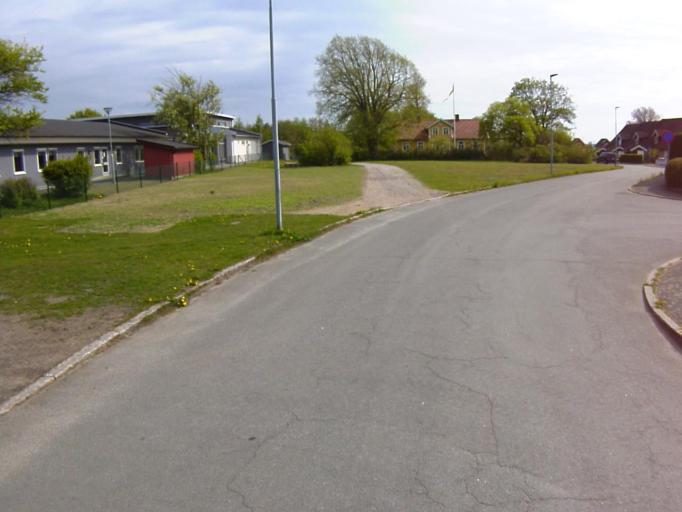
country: SE
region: Skane
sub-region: Kristianstads Kommun
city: Fjalkinge
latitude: 56.0440
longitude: 14.2702
